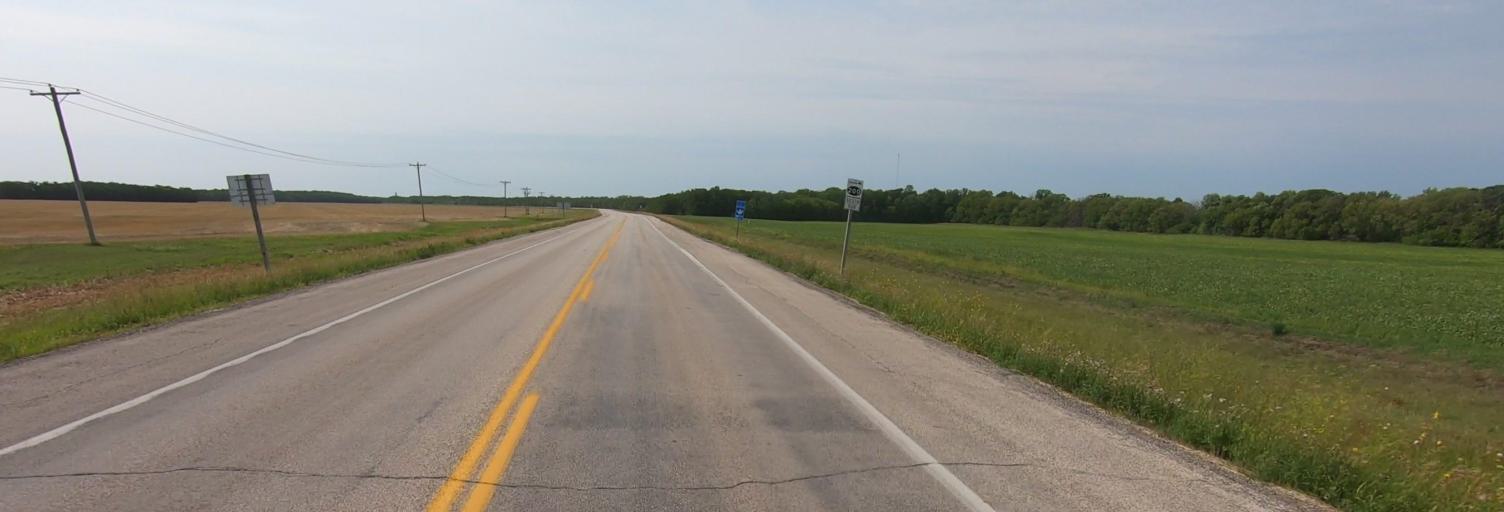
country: CA
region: Manitoba
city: Niverville
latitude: 49.6054
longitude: -97.1297
